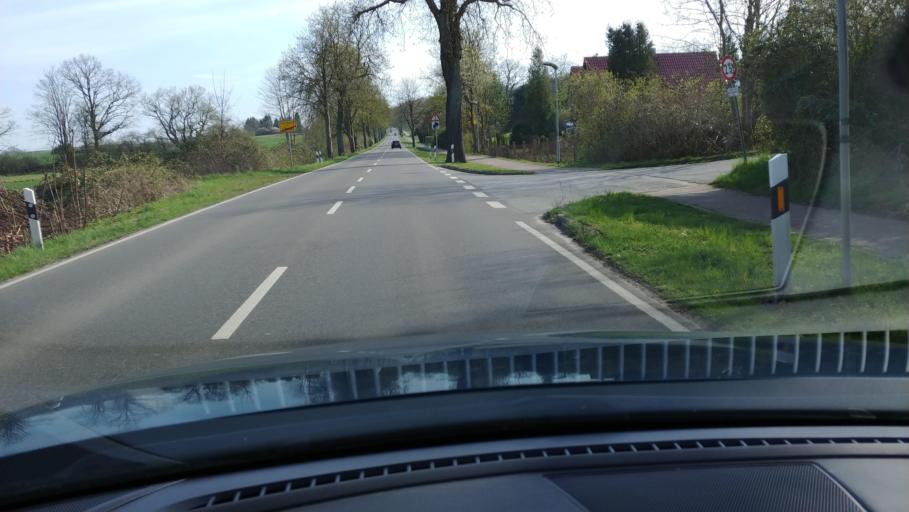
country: DE
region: Mecklenburg-Vorpommern
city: Lubstorf
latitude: 53.7256
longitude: 11.4024
